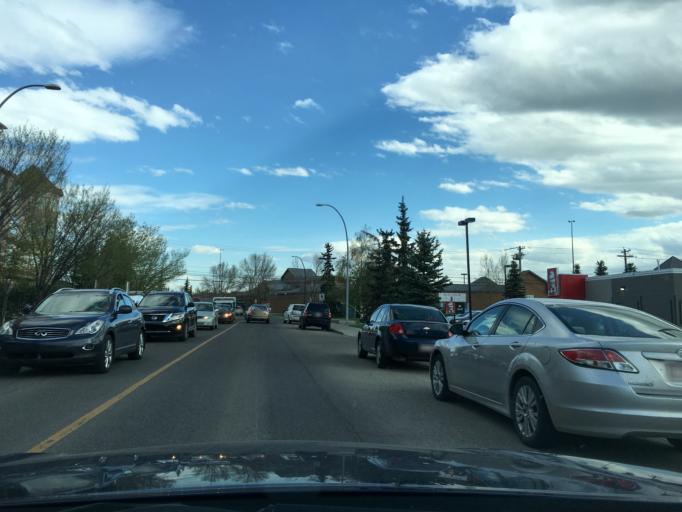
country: CA
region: Alberta
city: Calgary
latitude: 50.9159
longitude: -114.0669
